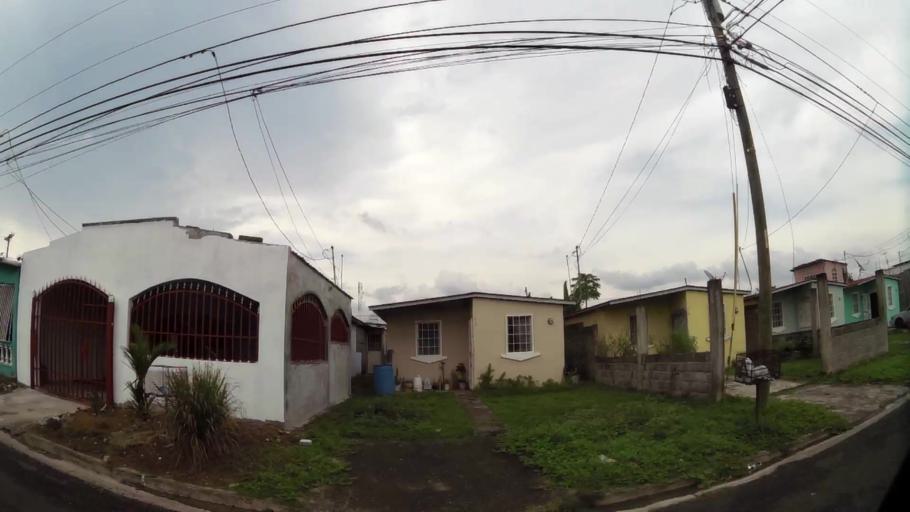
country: PA
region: Panama
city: Cabra Numero Uno
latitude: 9.0859
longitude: -79.3498
